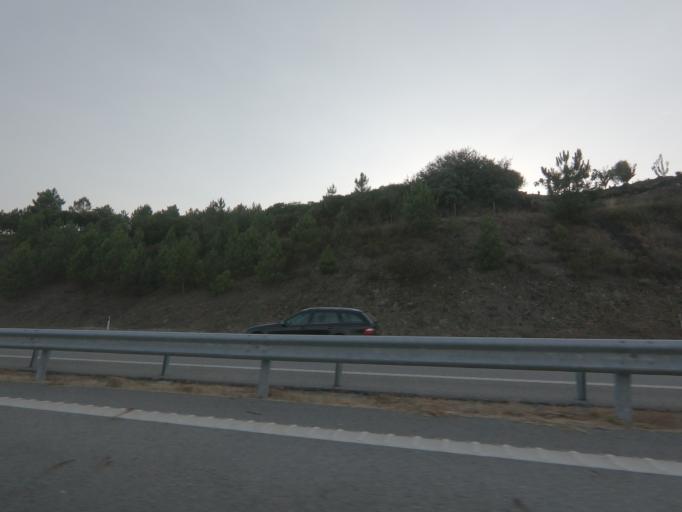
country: PT
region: Vila Real
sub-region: Santa Marta de Penaguiao
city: Santa Marta de Penaguiao
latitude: 41.2201
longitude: -7.7356
